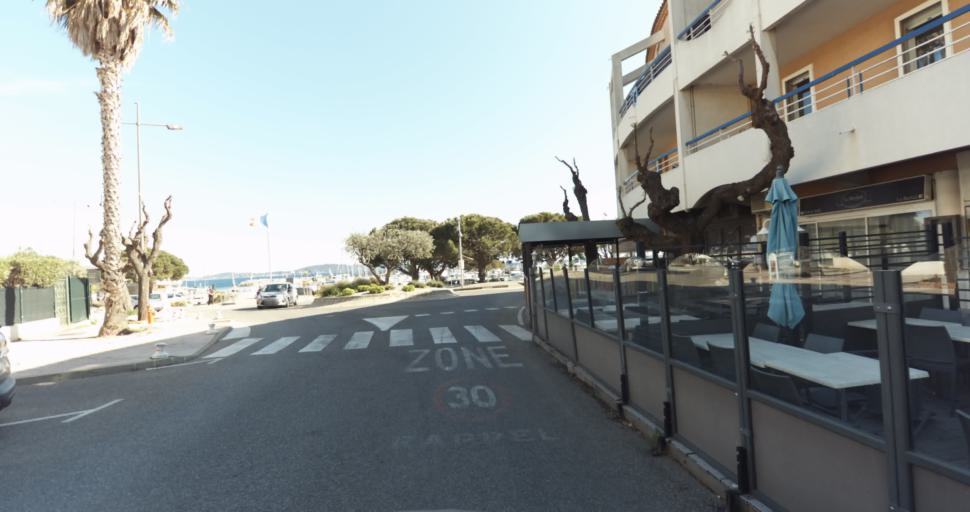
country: FR
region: Provence-Alpes-Cote d'Azur
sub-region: Departement du Var
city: Carqueiranne
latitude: 43.0884
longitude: 6.0774
